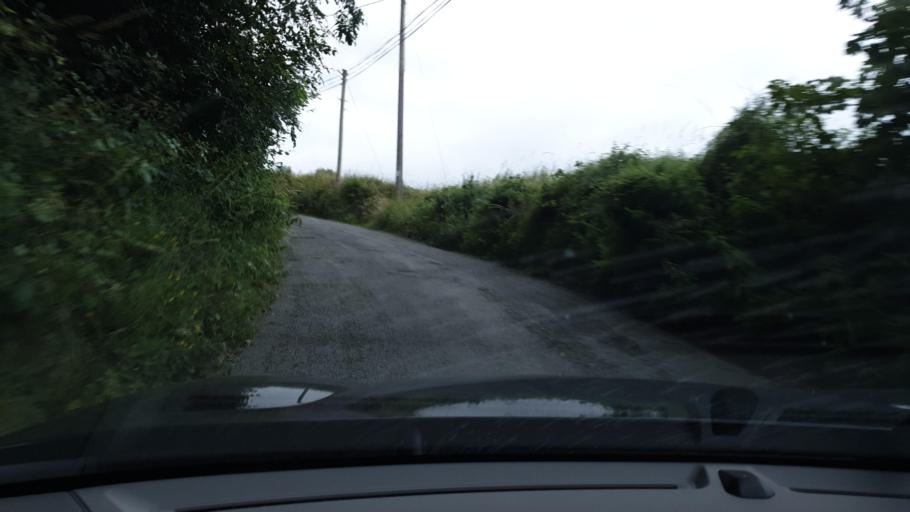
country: IE
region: Leinster
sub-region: South Dublin
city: Rathcoole
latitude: 53.2198
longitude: -6.4858
